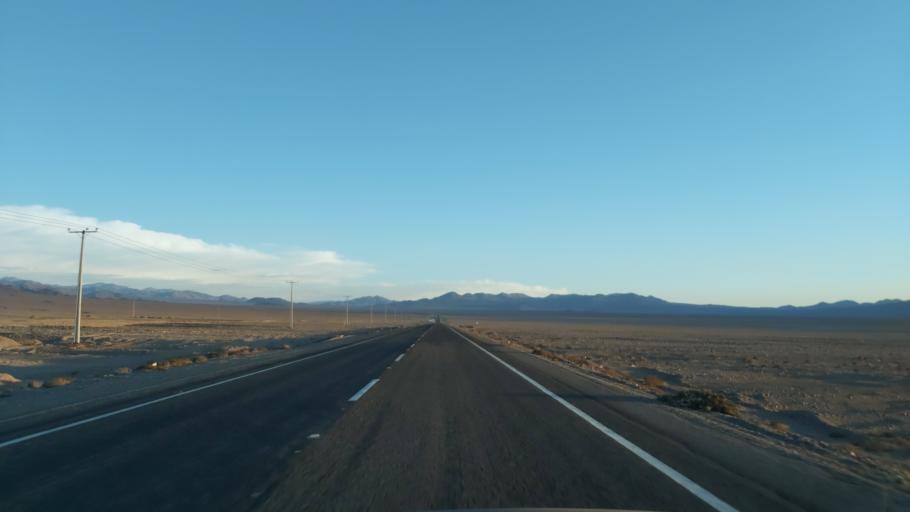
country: CL
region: Atacama
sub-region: Provincia de Chanaral
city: Diego de Almagro
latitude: -26.6203
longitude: -69.9518
